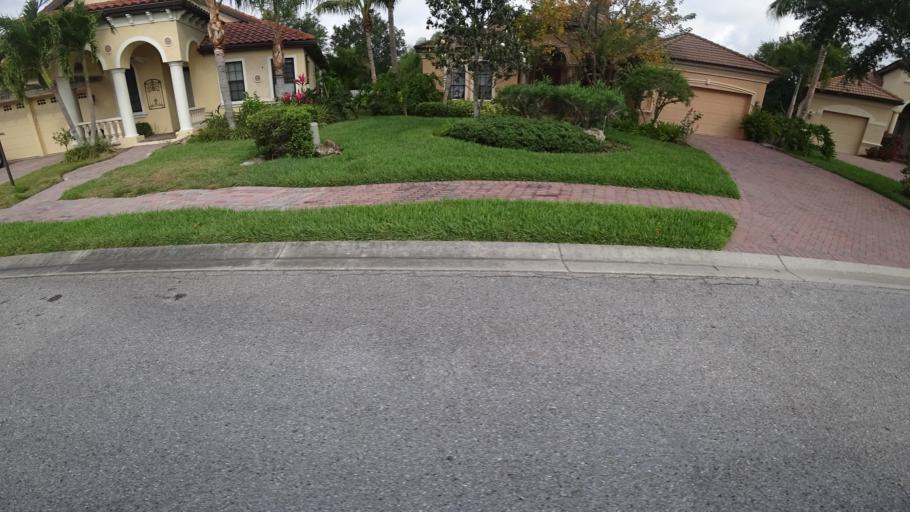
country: US
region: Florida
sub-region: Sarasota County
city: North Sarasota
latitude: 27.3974
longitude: -82.5183
